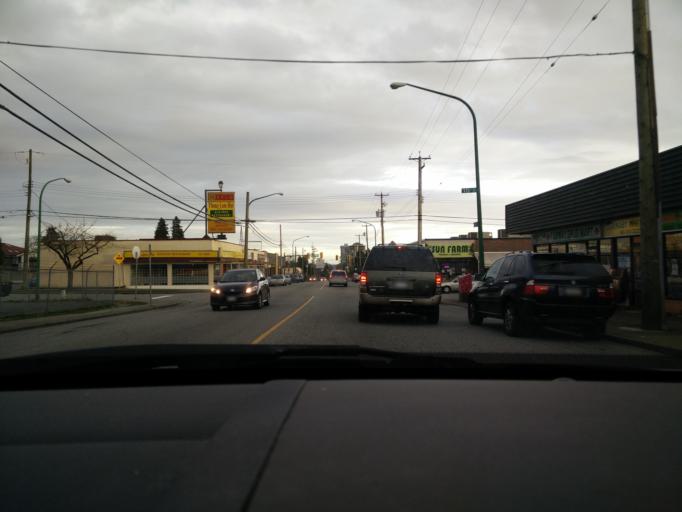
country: CA
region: British Columbia
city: New Westminster
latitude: 49.2228
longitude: -122.9325
